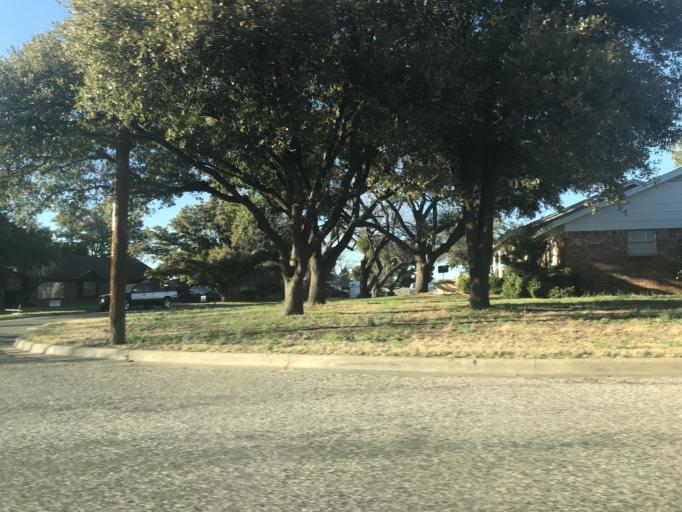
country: US
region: Texas
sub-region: Tom Green County
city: San Angelo
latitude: 31.4420
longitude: -100.4825
